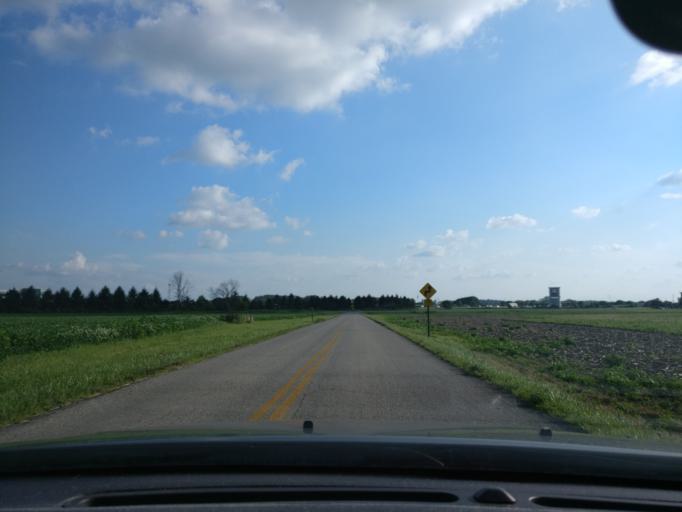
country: US
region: Ohio
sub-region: Clinton County
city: Wilmington
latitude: 39.5245
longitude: -83.8377
